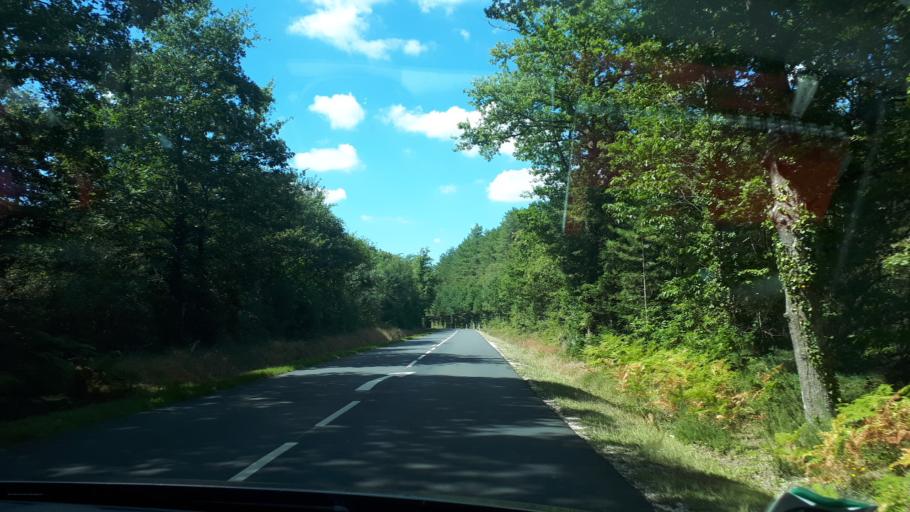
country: FR
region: Centre
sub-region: Departement du Loir-et-Cher
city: Neung-sur-Beuvron
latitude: 47.5485
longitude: 1.8670
